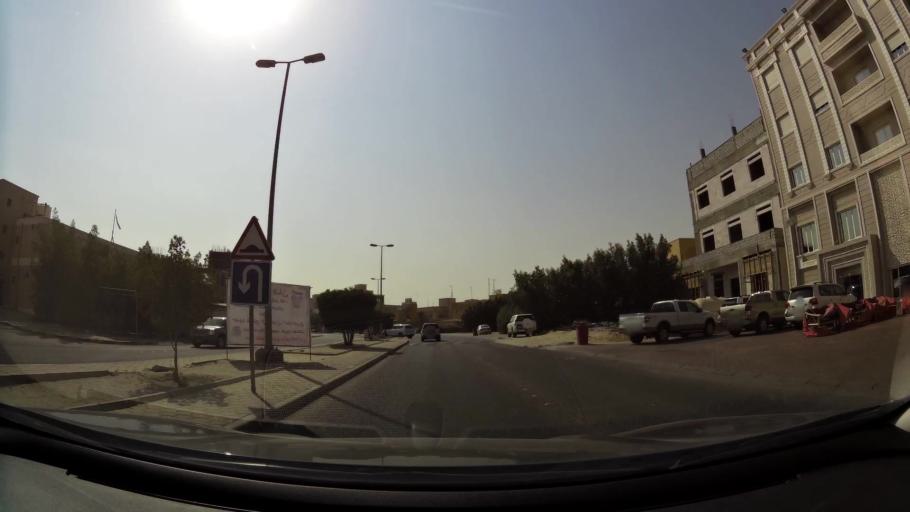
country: KW
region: Al Ahmadi
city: Al Fahahil
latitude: 29.0865
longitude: 48.1204
